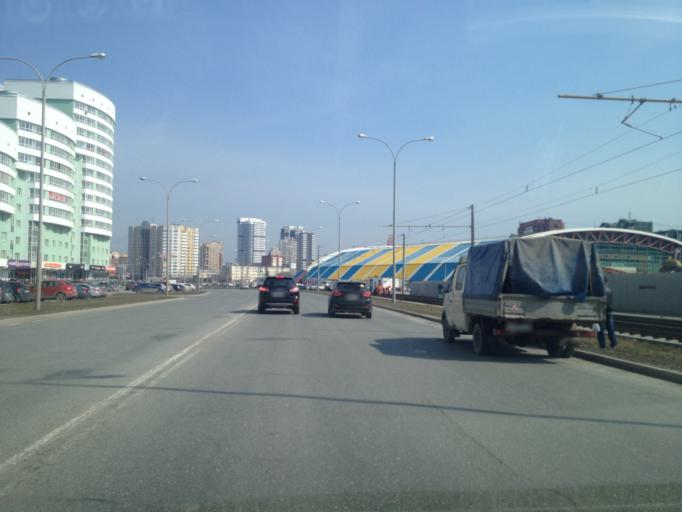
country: RU
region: Sverdlovsk
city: Yekaterinburg
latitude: 56.7976
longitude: 60.6221
